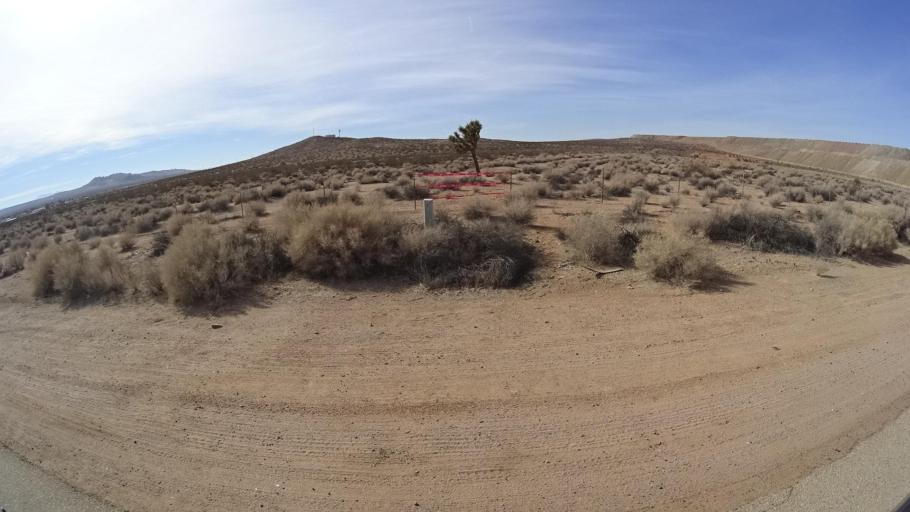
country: US
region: California
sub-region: Kern County
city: Boron
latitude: 35.0211
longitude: -117.6527
